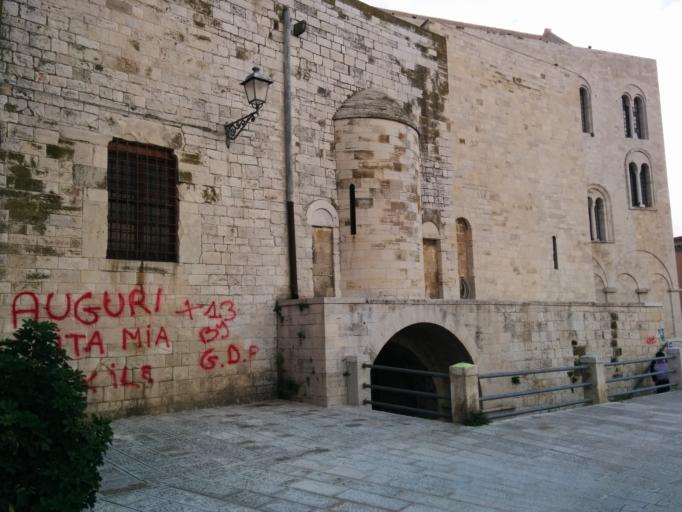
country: IT
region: Apulia
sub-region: Provincia di Bari
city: Bari
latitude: 41.1301
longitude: 16.8709
